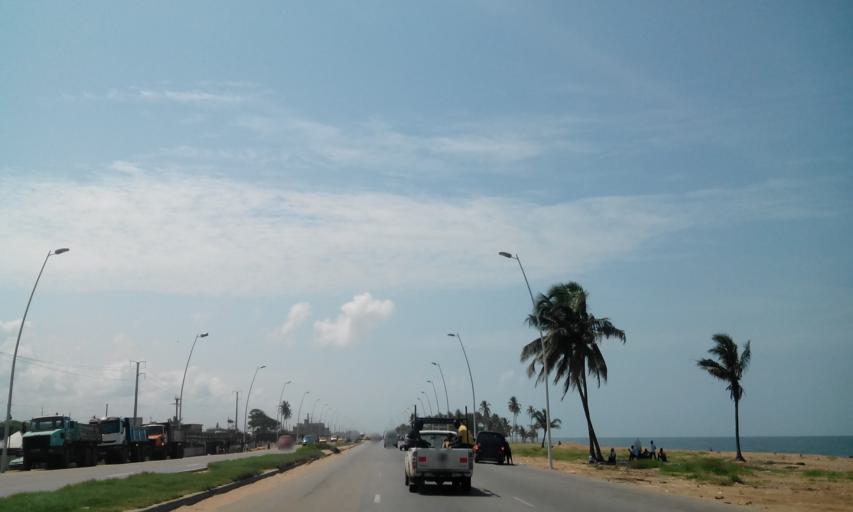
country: CI
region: Lagunes
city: Bingerville
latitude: 5.2398
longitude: -3.8996
